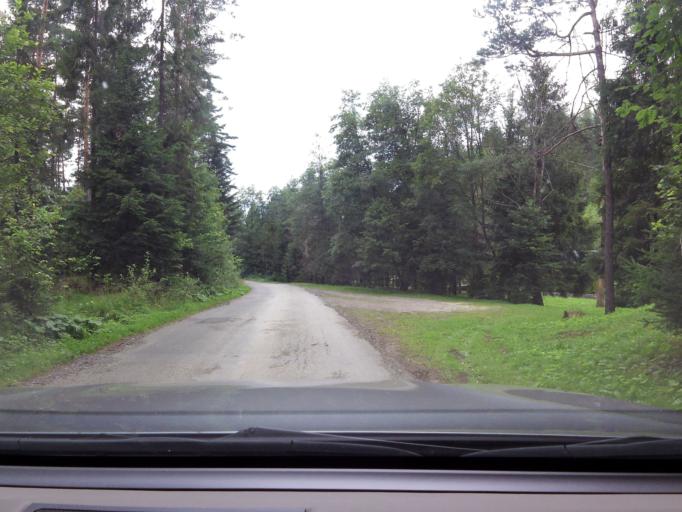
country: PL
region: Silesian Voivodeship
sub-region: Powiat zywiecki
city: Rajcza
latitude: 49.5015
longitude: 19.1280
